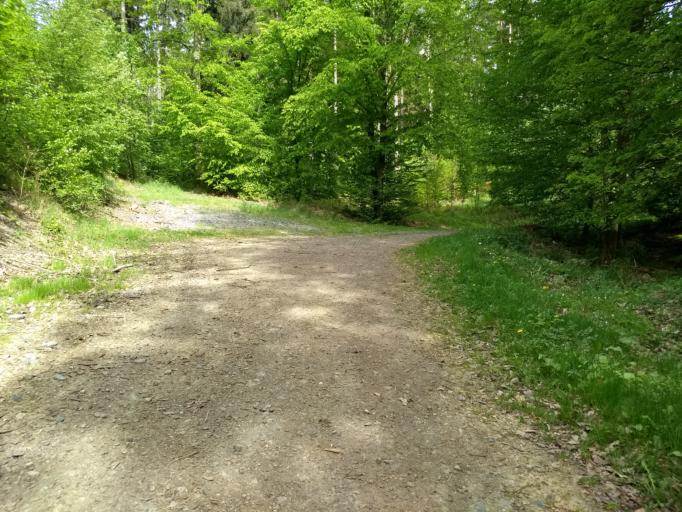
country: CZ
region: Central Bohemia
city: Unhost'
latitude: 50.0455
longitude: 14.1600
